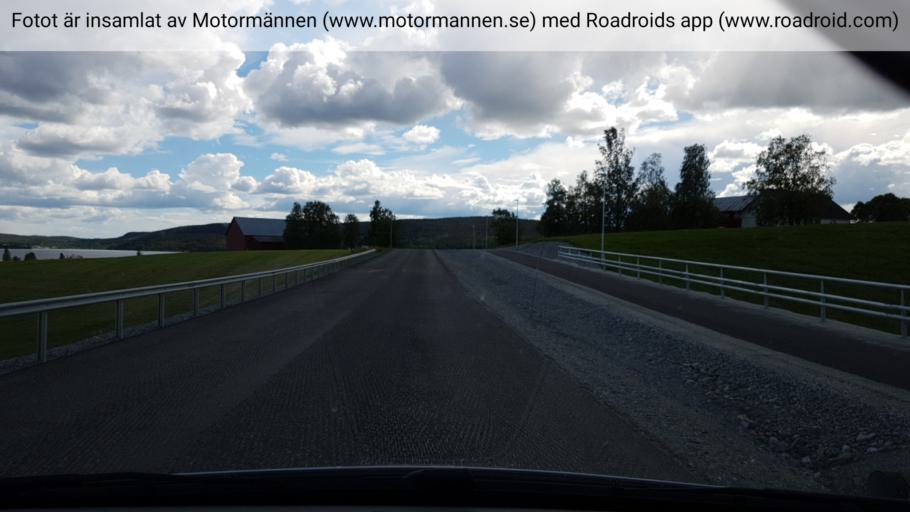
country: SE
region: Vaesterbotten
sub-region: Vannas Kommun
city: Vannasby
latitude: 64.0353
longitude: 20.0445
